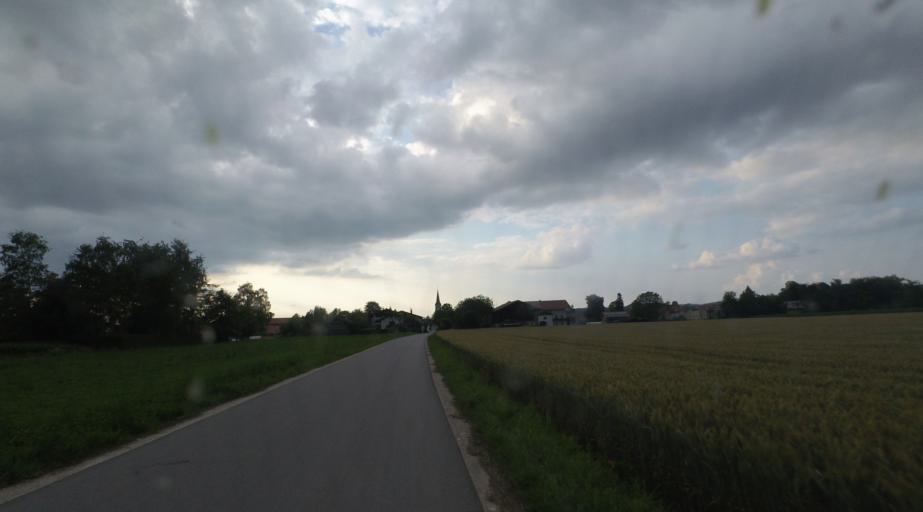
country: DE
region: Bavaria
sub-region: Upper Bavaria
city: Grabenstatt
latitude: 47.8397
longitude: 12.5431
